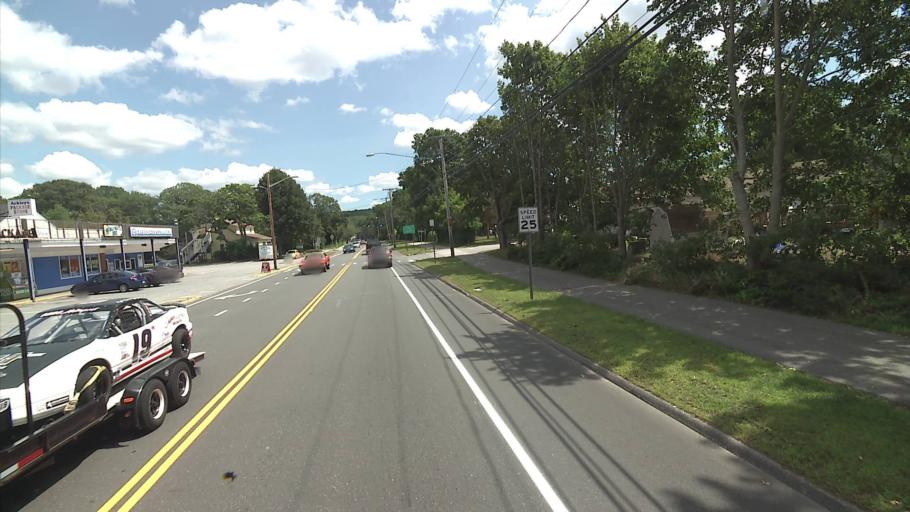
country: US
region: Connecticut
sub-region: New London County
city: Poquonock Bridge
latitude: 41.3463
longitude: -72.0278
